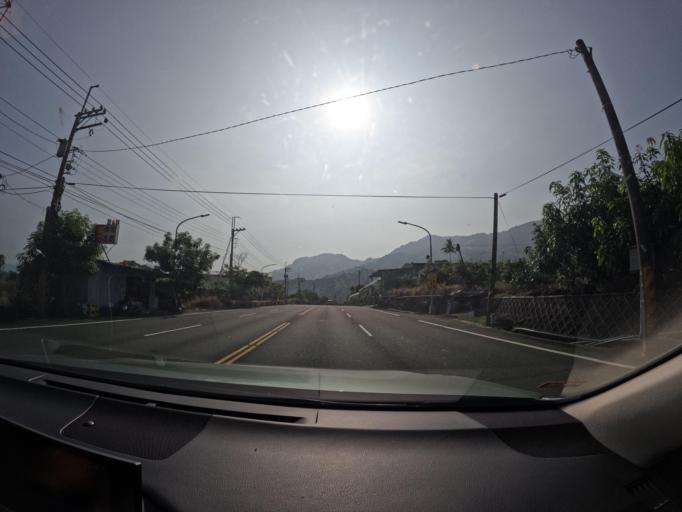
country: TW
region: Taiwan
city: Yujing
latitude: 23.0711
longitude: 120.5079
